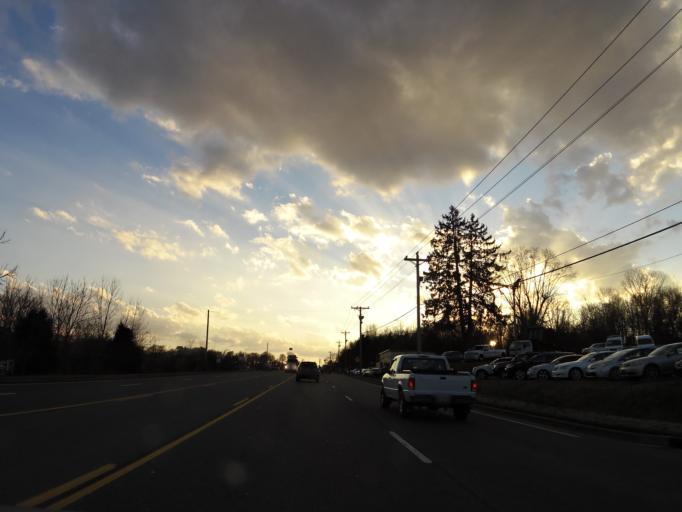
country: US
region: Tennessee
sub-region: Wilson County
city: Green Hill
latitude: 36.2276
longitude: -86.5373
